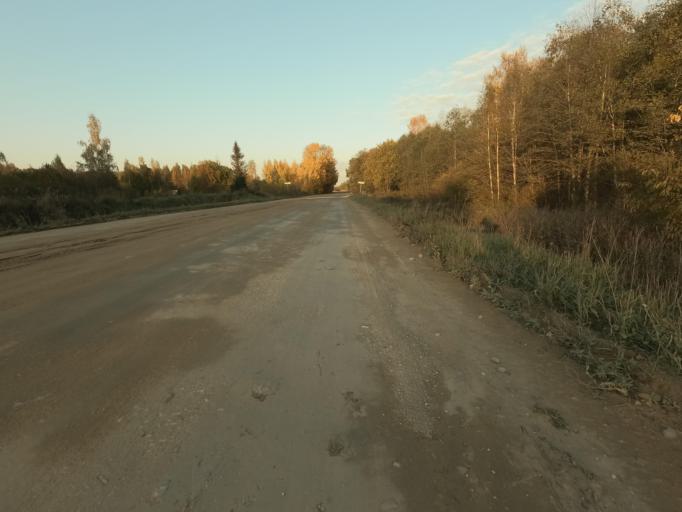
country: RU
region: Leningrad
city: Lyuban'
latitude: 59.0209
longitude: 31.0941
